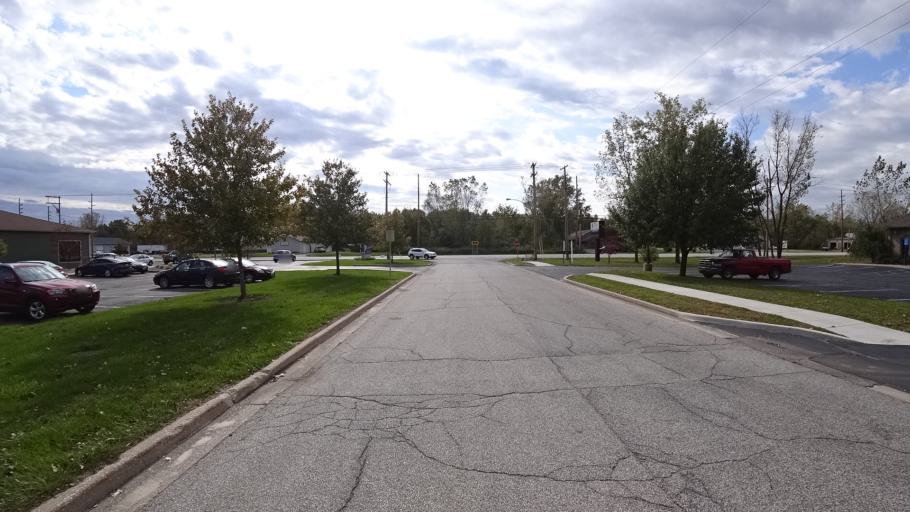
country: US
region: Indiana
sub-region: LaPorte County
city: Michigan City
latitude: 41.6664
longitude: -86.9006
